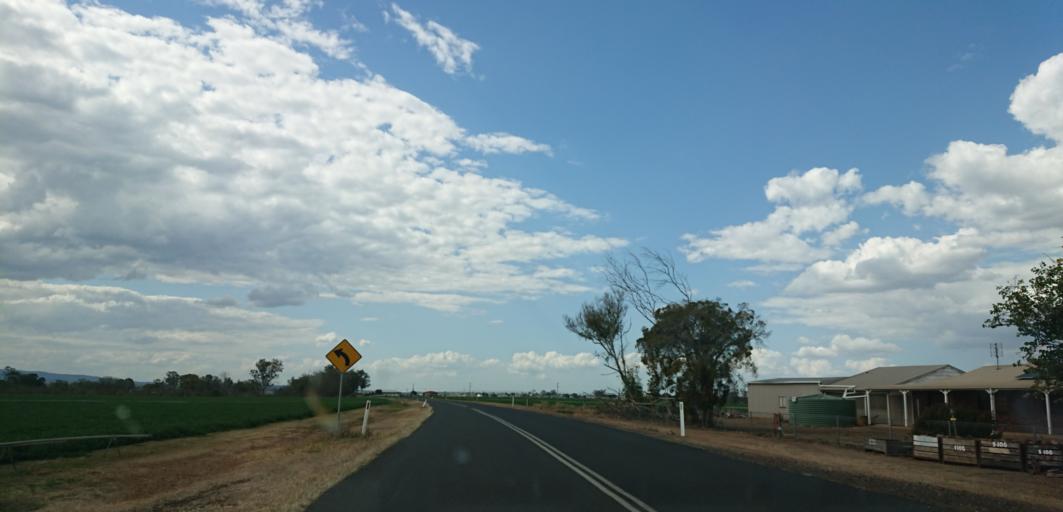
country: AU
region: Queensland
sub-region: Lockyer Valley
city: Gatton
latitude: -27.5970
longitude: 152.2228
